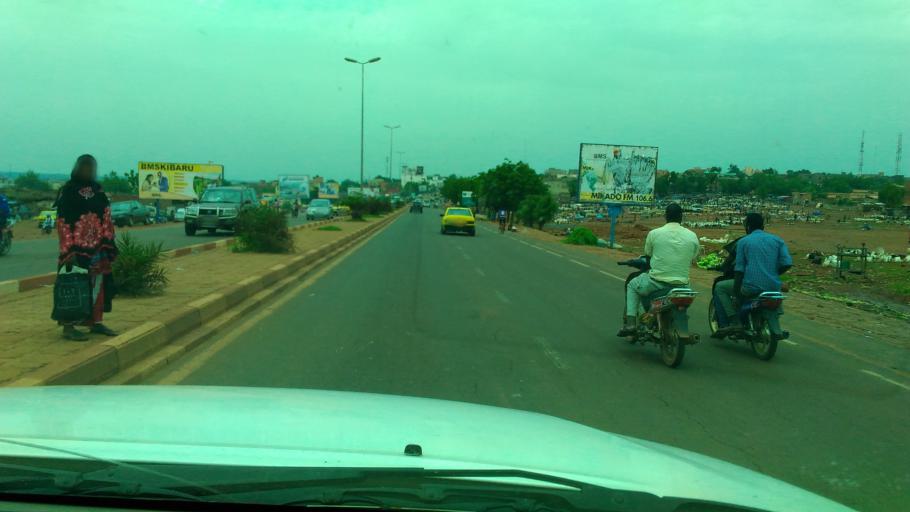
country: ML
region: Bamako
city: Bamako
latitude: 12.5971
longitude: -7.9928
